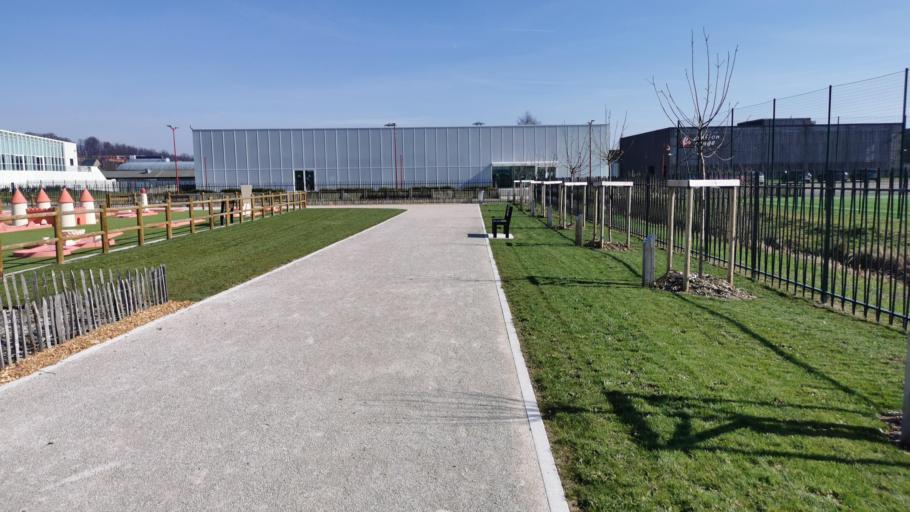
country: FR
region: Picardie
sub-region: Departement de la Somme
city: Flixecourt
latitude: 50.0141
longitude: 2.0740
